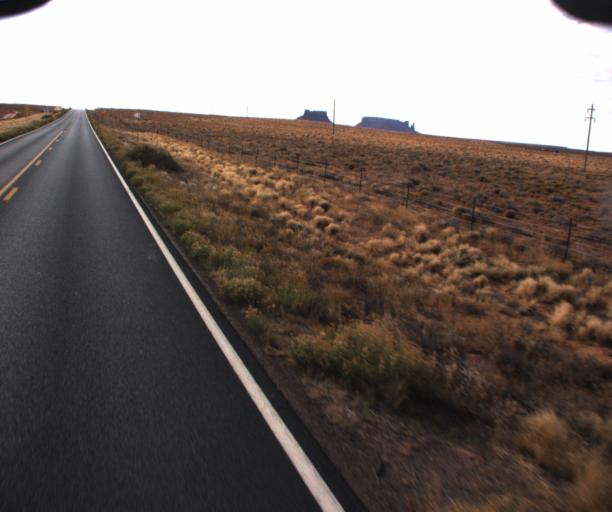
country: US
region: Arizona
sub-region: Apache County
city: Many Farms
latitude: 36.5876
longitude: -109.5599
